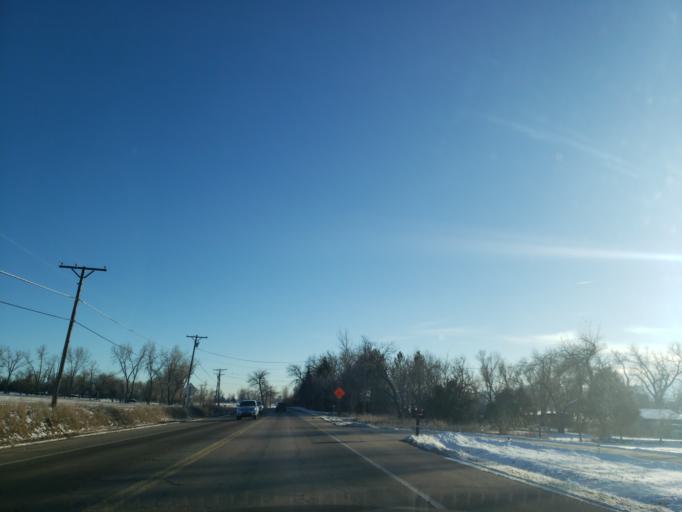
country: US
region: Colorado
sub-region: Larimer County
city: Fort Collins
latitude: 40.6222
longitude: -105.0721
